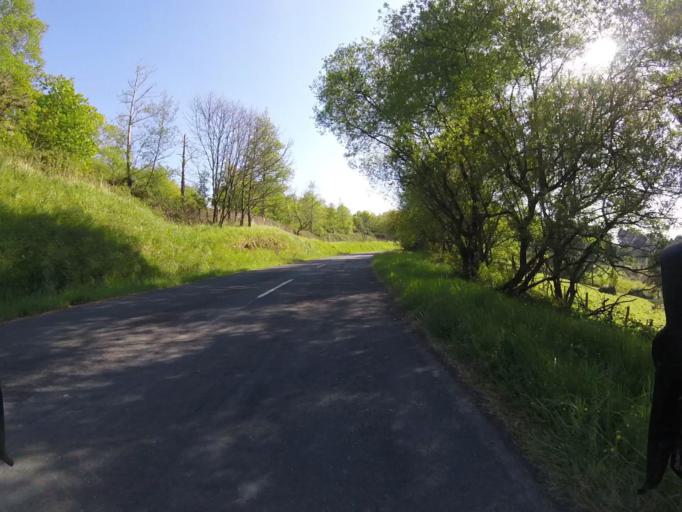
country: ES
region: Basque Country
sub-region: Provincia de Guipuzcoa
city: Fuenterrabia
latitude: 43.3612
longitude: -1.8349
